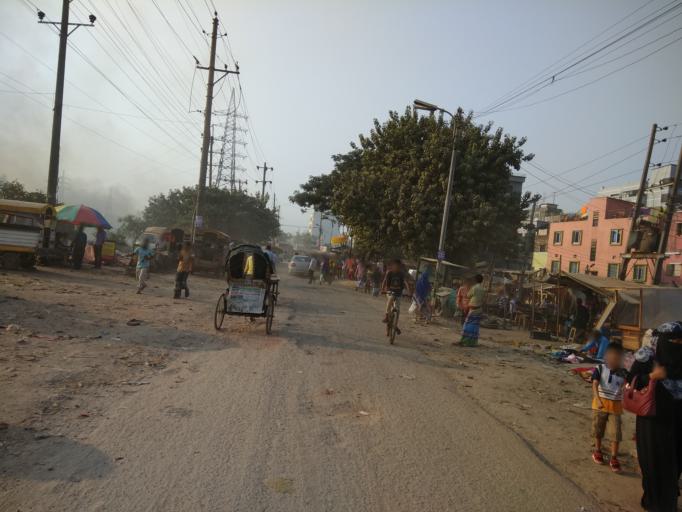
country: BD
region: Dhaka
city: Azimpur
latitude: 23.7219
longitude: 90.3754
